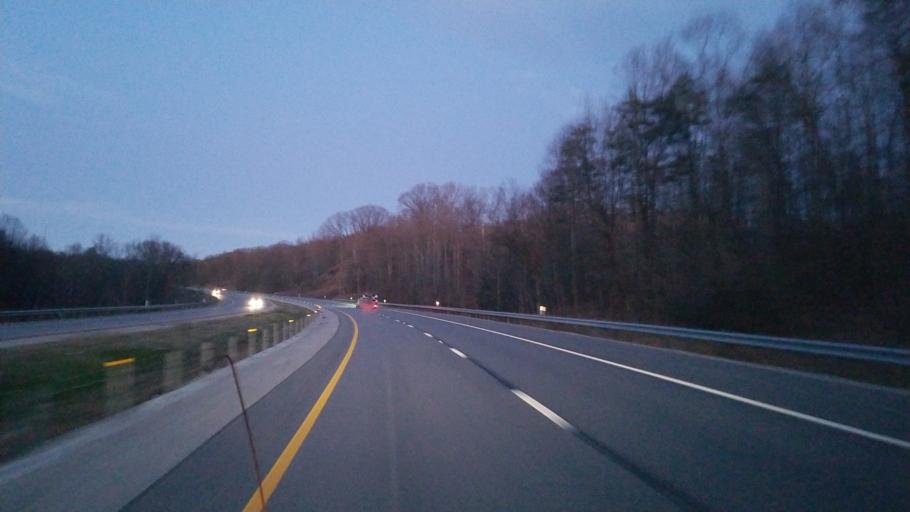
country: US
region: West Virginia
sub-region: Jackson County
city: Ravenswood
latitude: 39.0230
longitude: -81.6119
